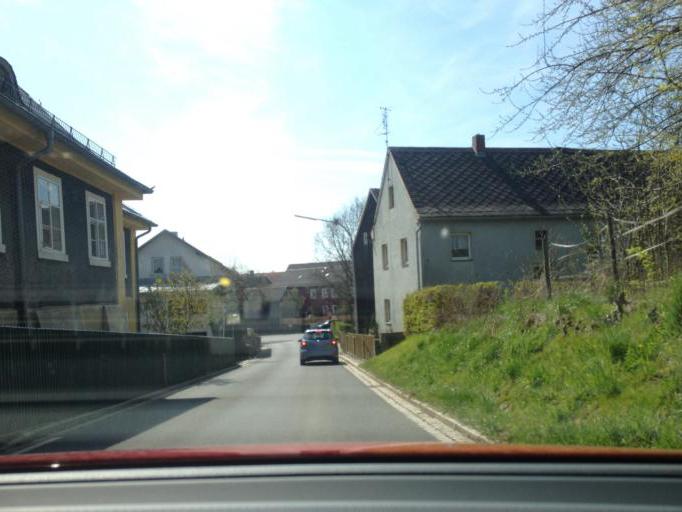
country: DE
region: Bavaria
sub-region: Upper Franconia
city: Thiersheim
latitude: 50.0683
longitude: 12.1513
